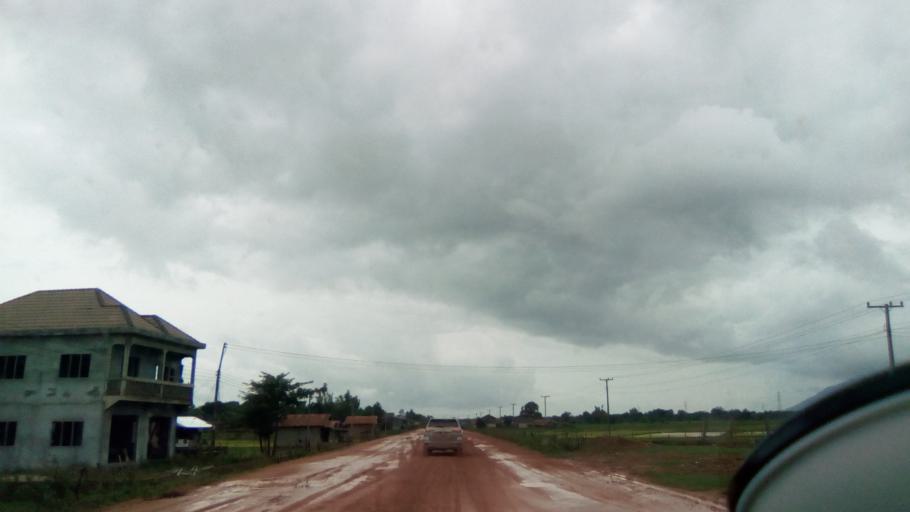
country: LA
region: Attapu
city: Attapu
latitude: 14.7378
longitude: 106.6879
